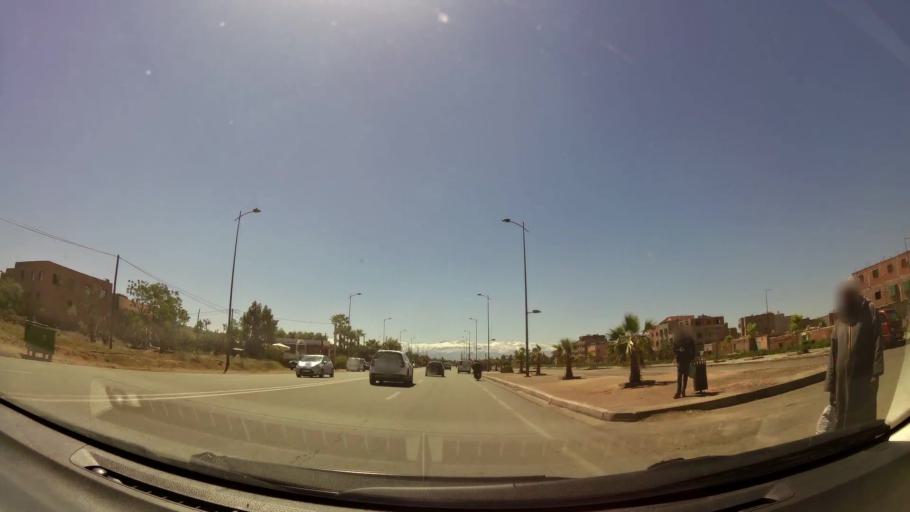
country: MA
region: Marrakech-Tensift-Al Haouz
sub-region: Marrakech
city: Marrakesh
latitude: 31.5624
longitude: -7.9791
